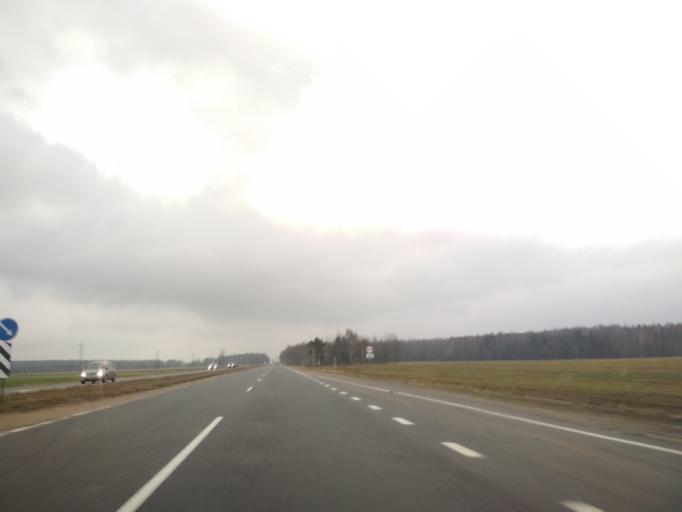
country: BY
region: Minsk
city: Dukora
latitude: 53.6317
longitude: 28.0206
